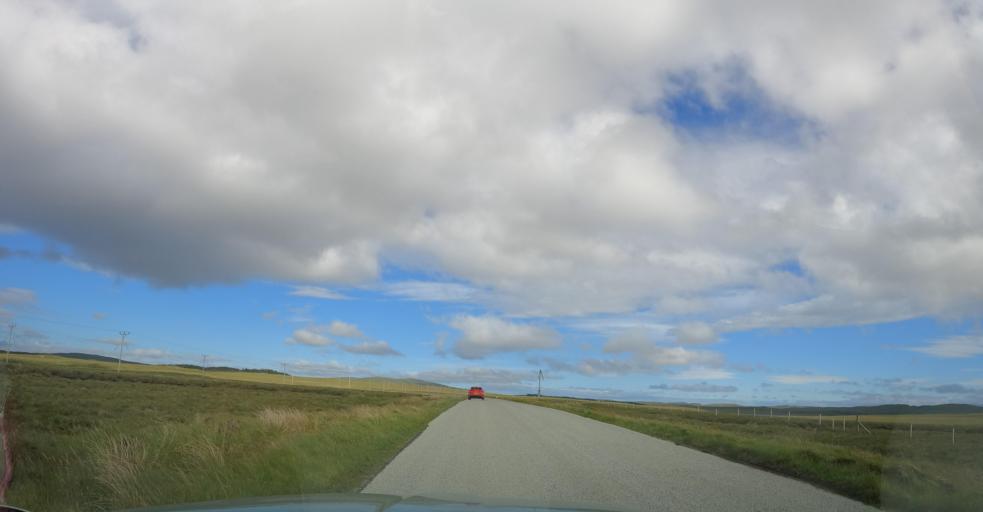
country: GB
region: Scotland
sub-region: Eilean Siar
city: Isle of Lewis
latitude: 58.1870
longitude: -6.6884
